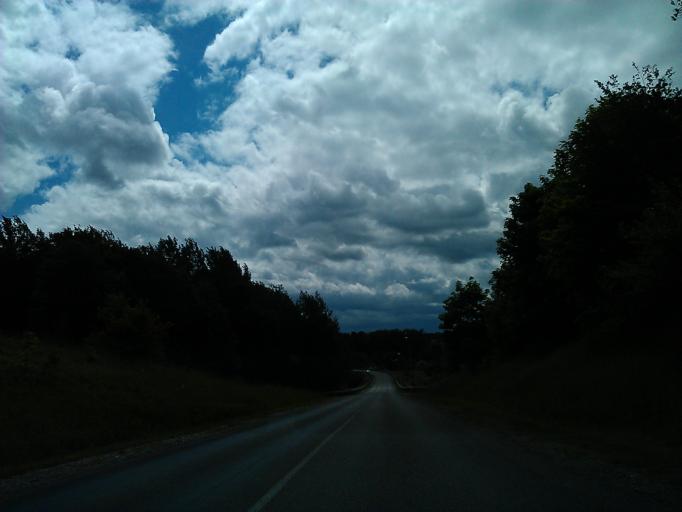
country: LV
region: Talsu Rajons
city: Stende
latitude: 57.0754
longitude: 22.2912
